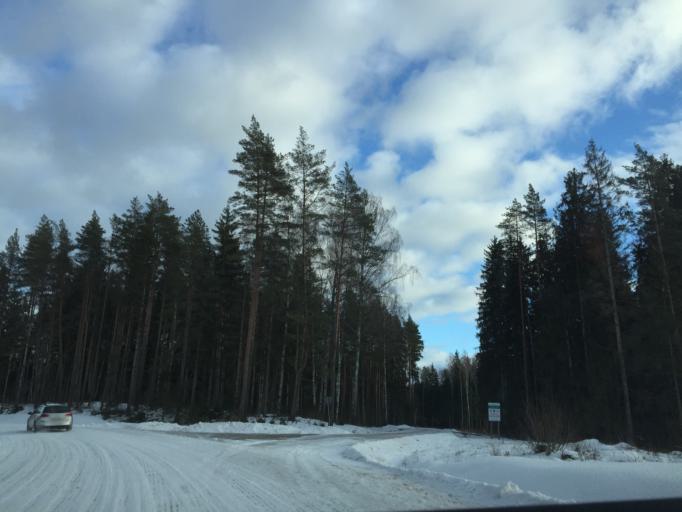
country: LV
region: Ogre
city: Jumprava
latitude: 56.5496
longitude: 24.8934
